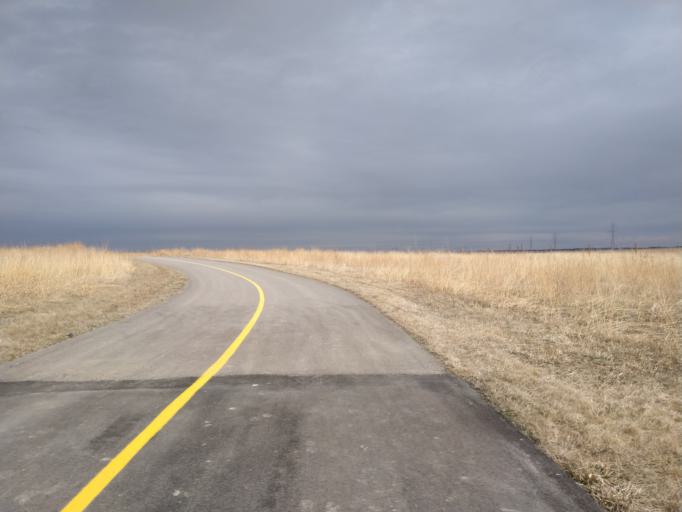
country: CA
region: Alberta
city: Airdrie
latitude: 51.1784
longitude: -114.0404
